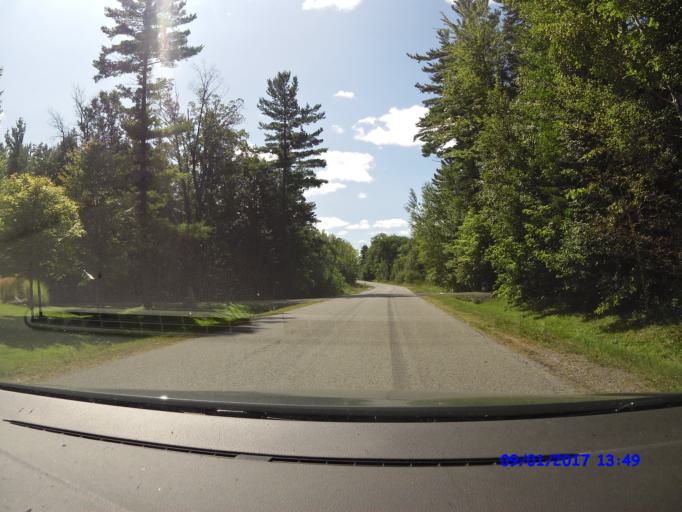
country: CA
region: Ontario
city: Bells Corners
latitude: 45.3696
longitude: -75.9648
